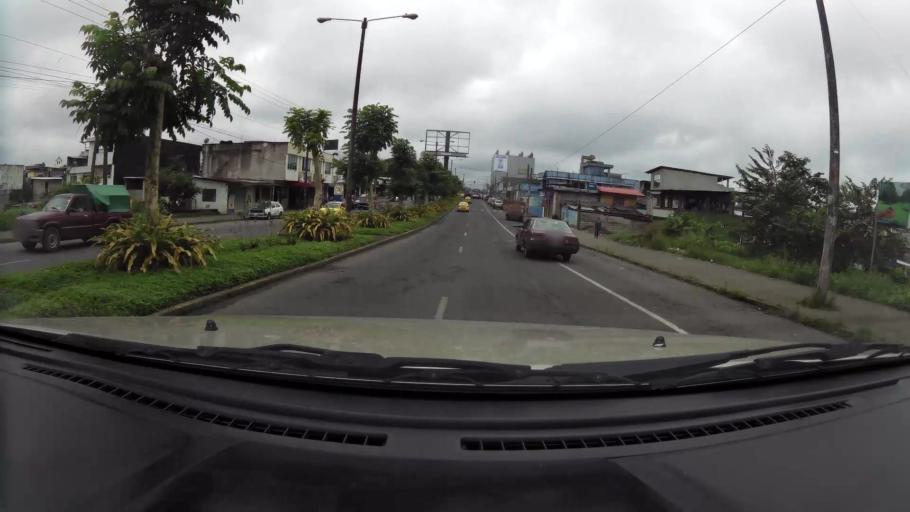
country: EC
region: Santo Domingo de los Tsachilas
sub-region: Canton Santo Domingo de los Colorados
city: Santo Domingo de los Colorados
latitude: -0.2609
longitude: -79.1812
